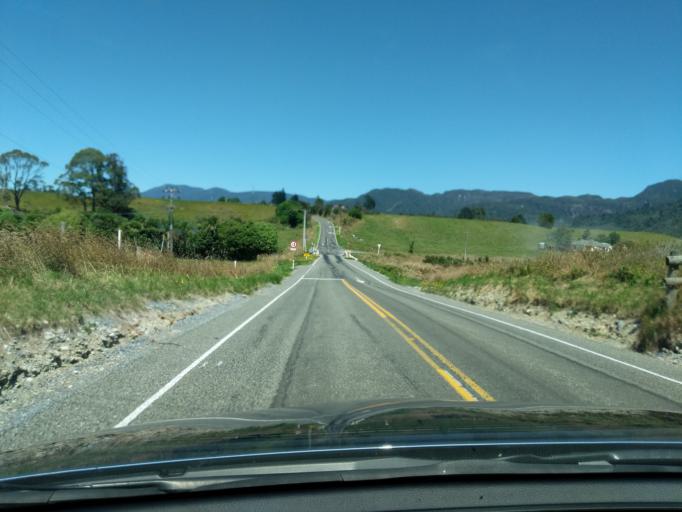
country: NZ
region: Tasman
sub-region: Tasman District
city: Takaka
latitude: -40.6866
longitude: 172.6518
